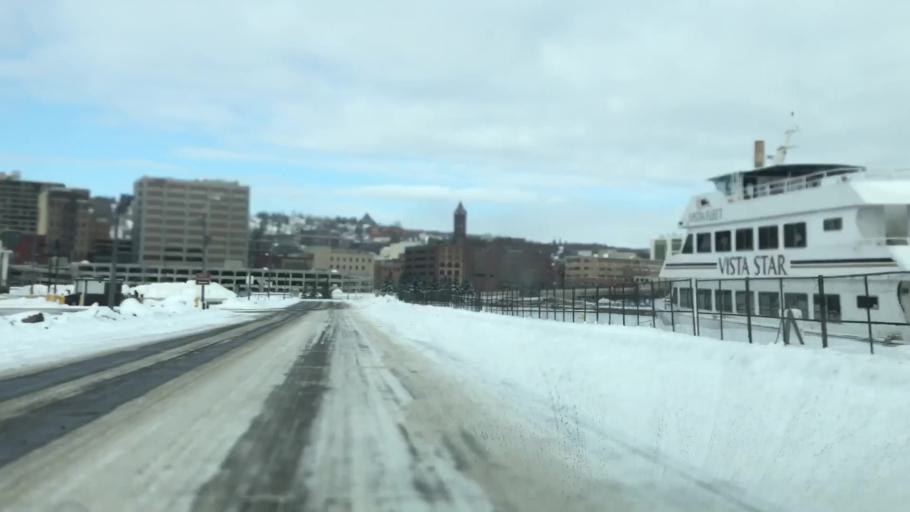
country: US
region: Minnesota
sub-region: Saint Louis County
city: Duluth
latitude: 46.7821
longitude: -92.0972
